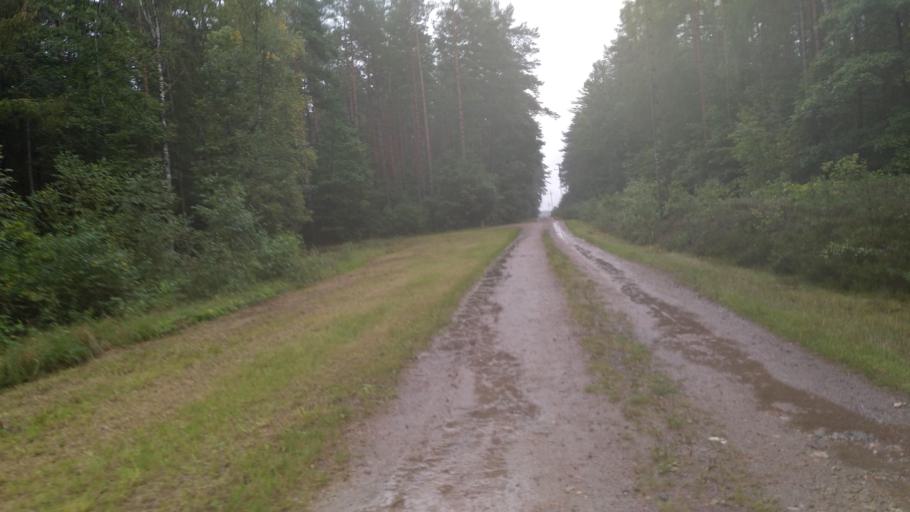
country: PL
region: Pomeranian Voivodeship
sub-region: Powiat wejherowski
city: Goscicino
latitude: 54.6202
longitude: 18.1529
